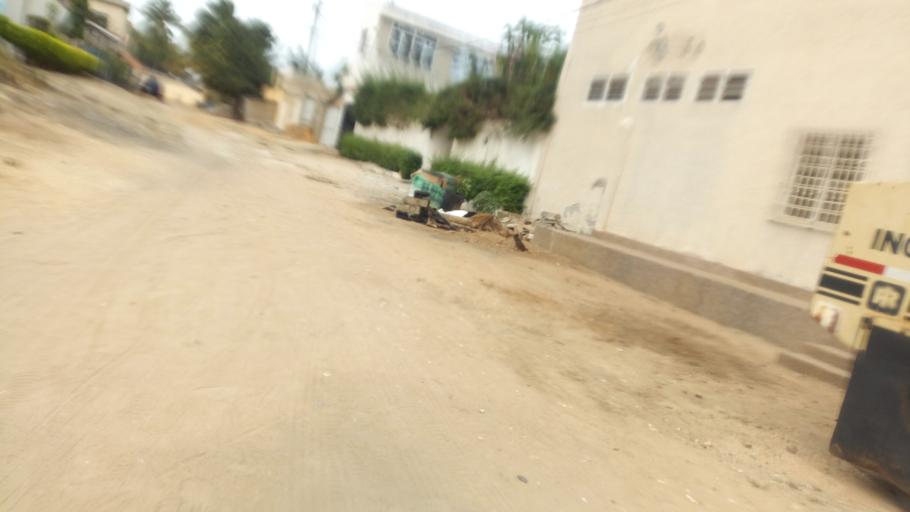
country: TG
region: Maritime
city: Lome
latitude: 6.2054
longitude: 1.1912
